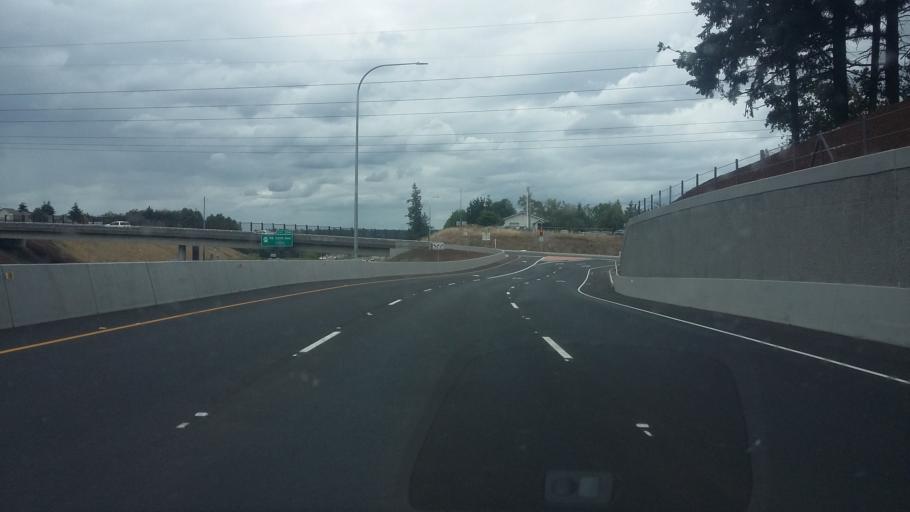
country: US
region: Washington
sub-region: Clark County
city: Orchards
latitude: 45.6341
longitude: -122.5598
